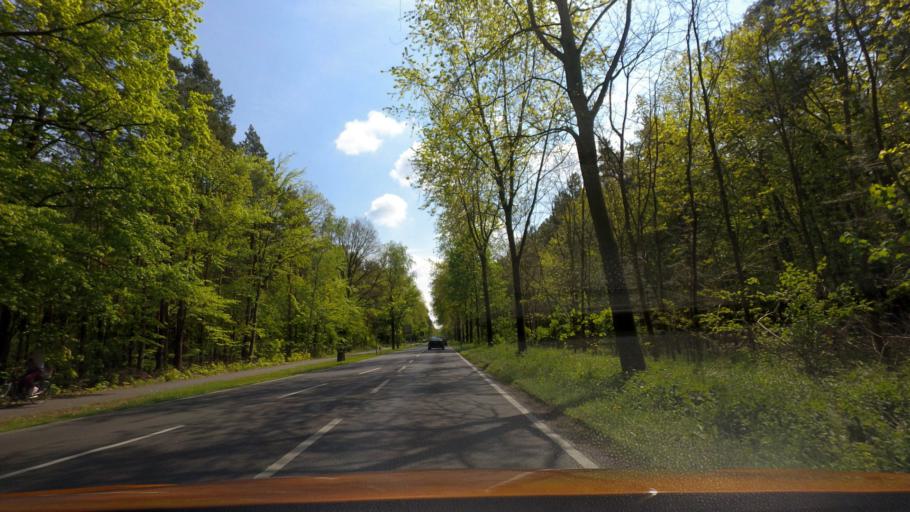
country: DE
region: Berlin
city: Grunau
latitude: 52.4051
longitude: 13.5900
